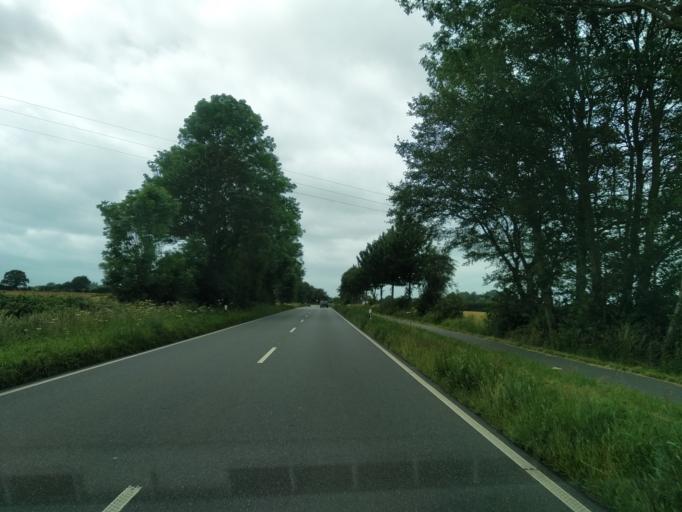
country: DE
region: Schleswig-Holstein
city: Ringsberg
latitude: 54.8050
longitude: 9.5918
